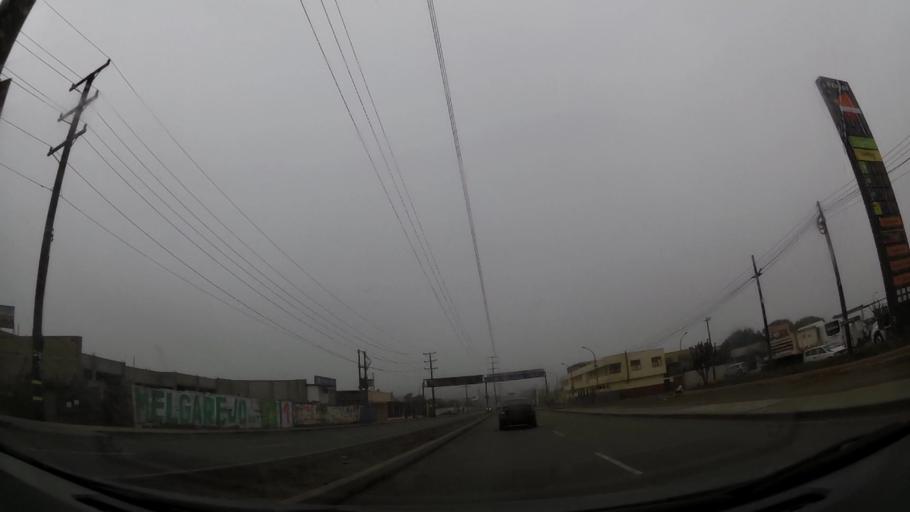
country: PE
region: Lima
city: Ventanilla
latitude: -11.8405
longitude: -77.1138
